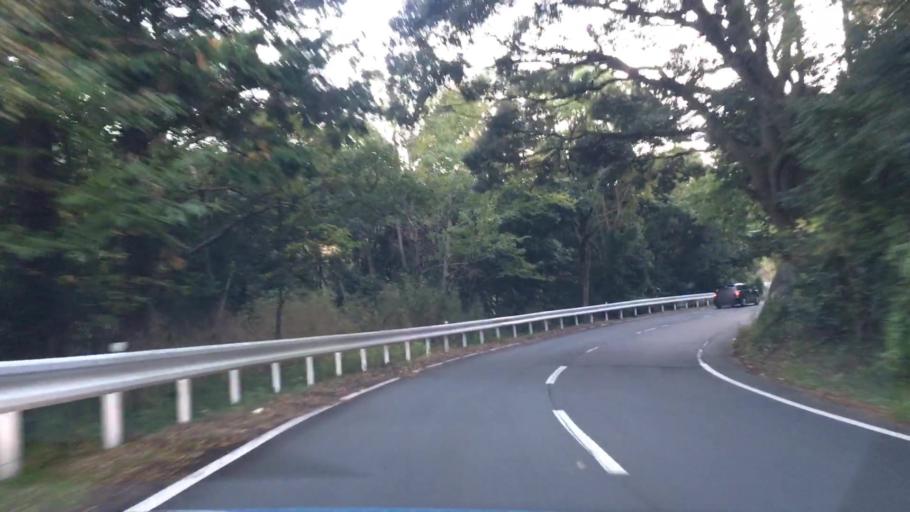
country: JP
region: Shizuoka
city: Heda
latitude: 35.0097
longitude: 138.8353
